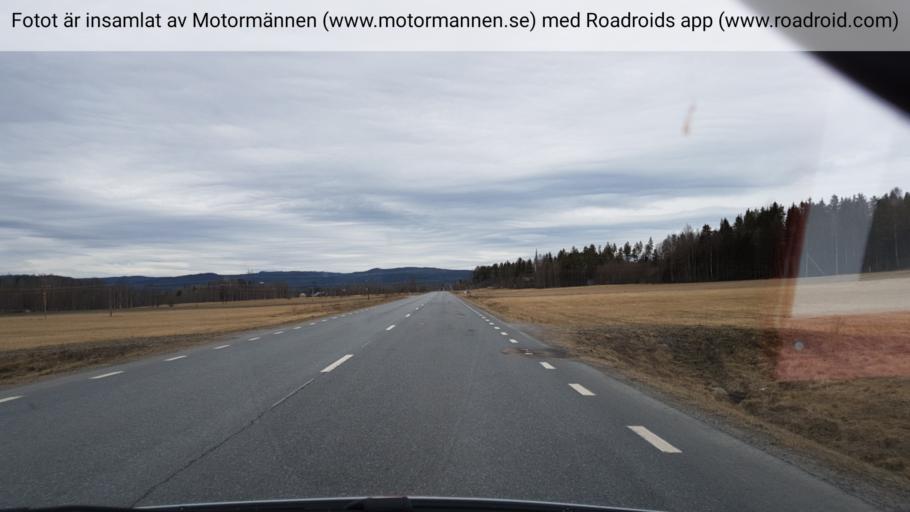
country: SE
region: Vaesternorrland
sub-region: Solleftea Kommun
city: Solleftea
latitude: 63.2255
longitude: 17.2190
